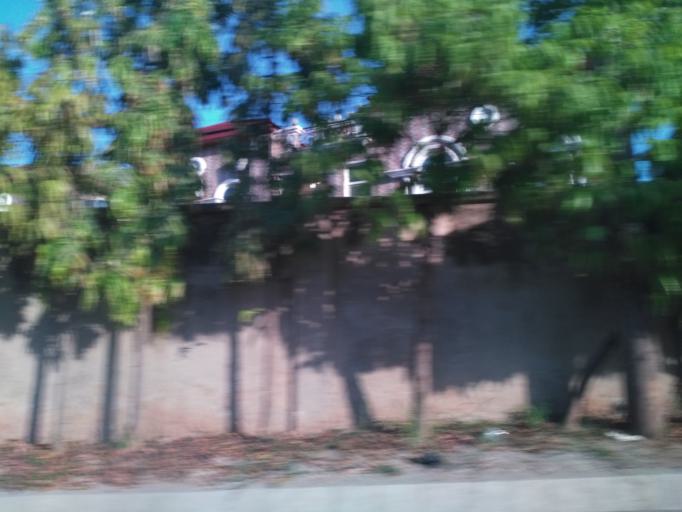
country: TZ
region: Dar es Salaam
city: Magomeni
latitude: -6.7643
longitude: 39.2610
